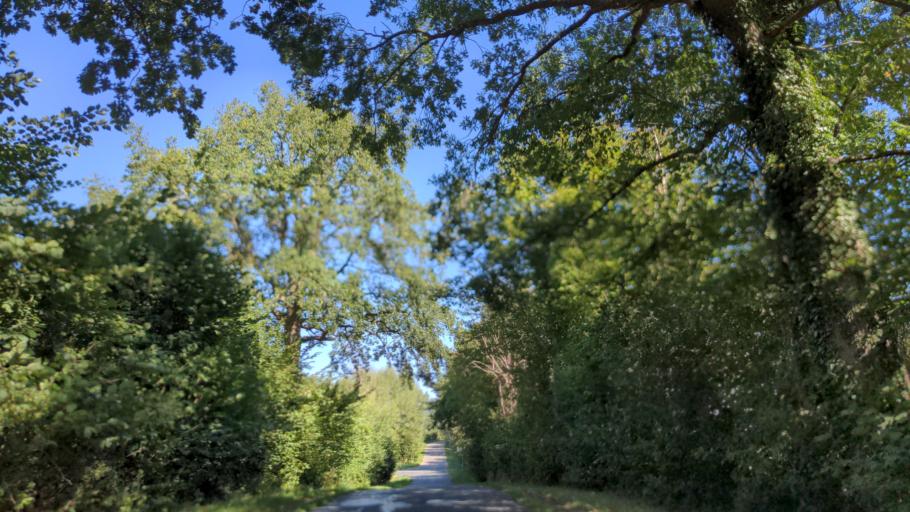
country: DE
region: Schleswig-Holstein
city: Gross Disnack
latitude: 53.7509
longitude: 10.6883
